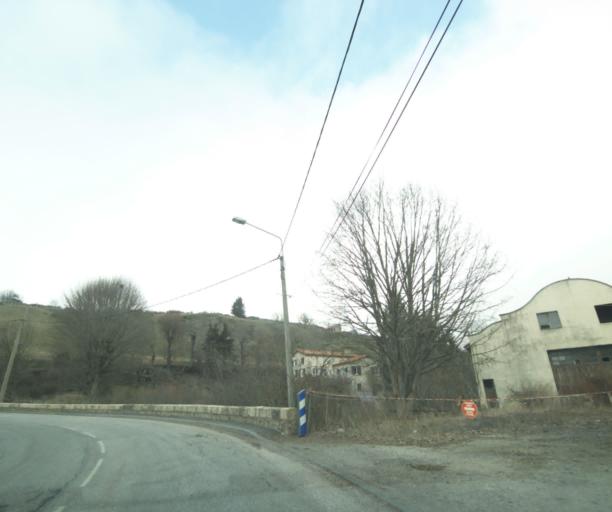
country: FR
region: Languedoc-Roussillon
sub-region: Departement de la Lozere
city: Langogne
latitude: 44.7696
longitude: 3.8865
